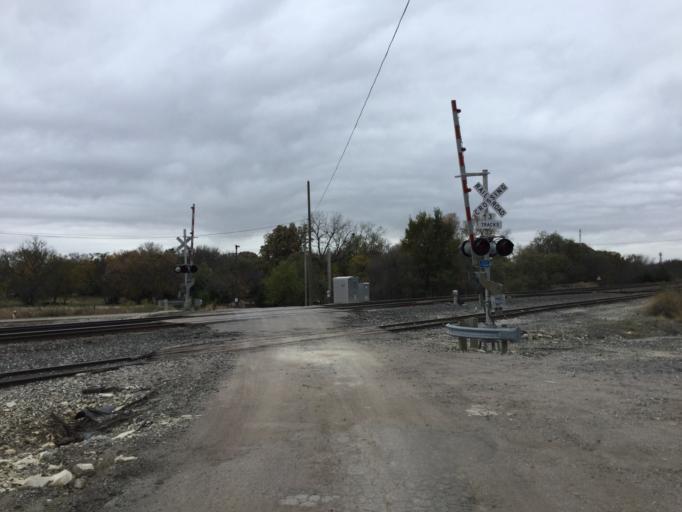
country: US
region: Kansas
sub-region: Butler County
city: El Dorado
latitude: 37.8003
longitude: -96.8621
